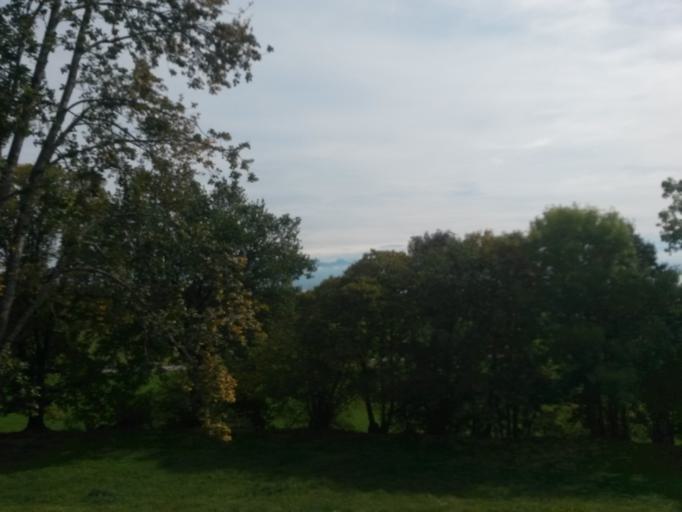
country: CH
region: Vaud
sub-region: Nyon District
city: Arzier
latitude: 46.4603
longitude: 6.2219
